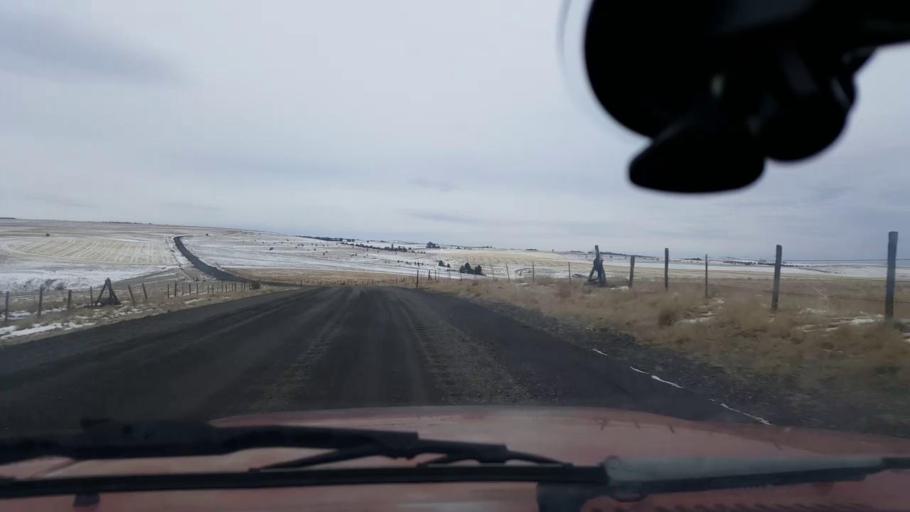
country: US
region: Washington
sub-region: Garfield County
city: Pomeroy
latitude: 46.3201
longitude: -117.4142
